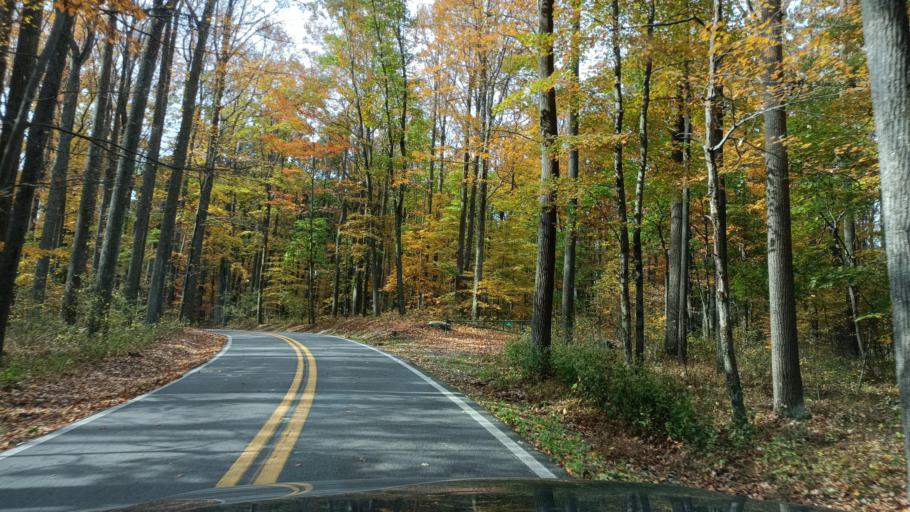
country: US
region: West Virginia
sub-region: Monongalia County
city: Cheat Lake
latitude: 39.6465
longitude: -79.7911
